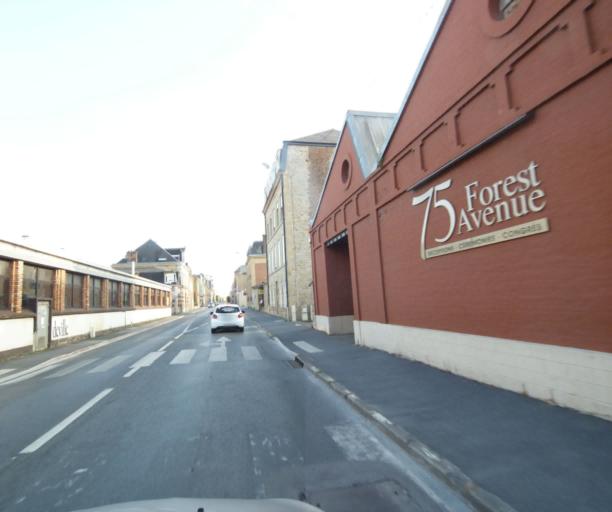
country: FR
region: Champagne-Ardenne
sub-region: Departement des Ardennes
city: Charleville-Mezieres
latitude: 49.7747
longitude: 4.7273
